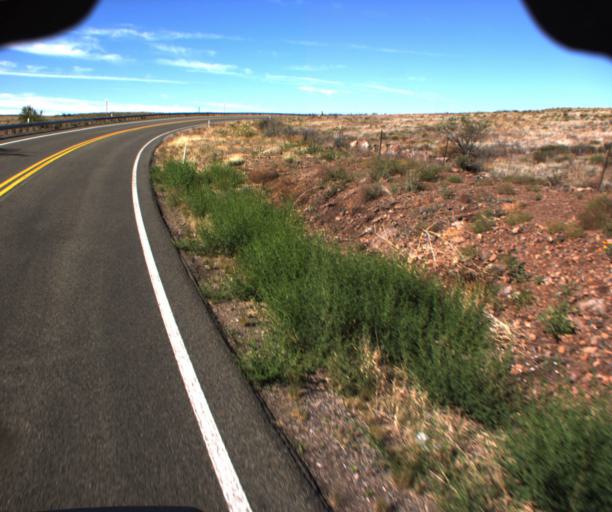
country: US
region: Arizona
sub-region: Yavapai County
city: Congress
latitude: 34.3312
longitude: -112.6871
